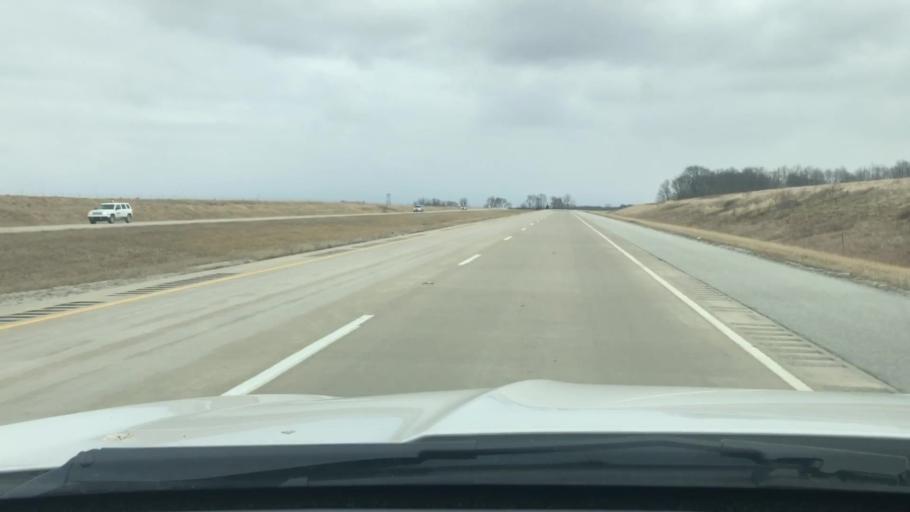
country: US
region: Indiana
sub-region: Carroll County
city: Delphi
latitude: 40.6218
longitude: -86.6300
